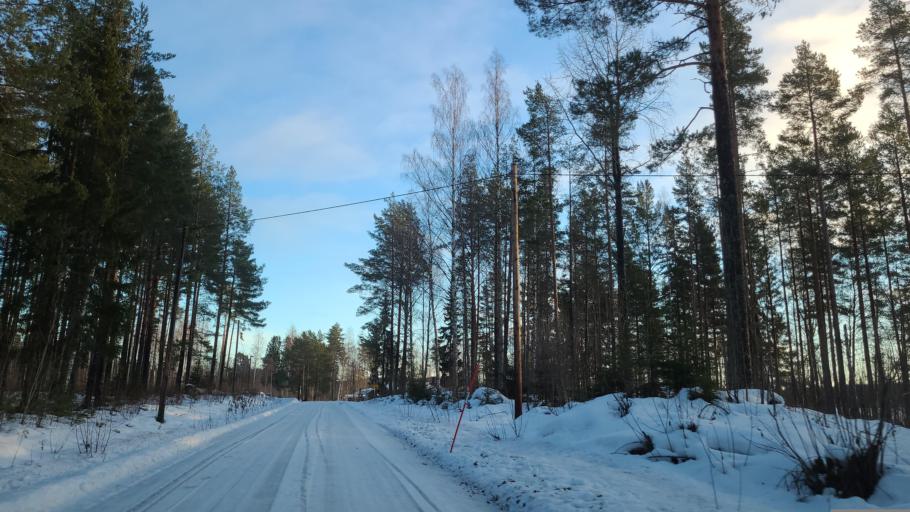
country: SE
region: Gaevleborg
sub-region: Bollnas Kommun
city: Kilafors
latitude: 61.3992
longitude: 16.6548
